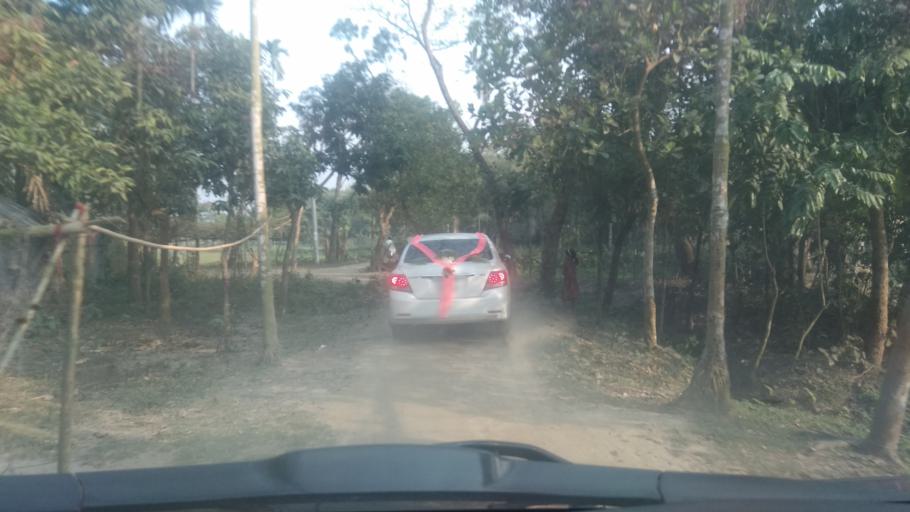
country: BD
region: Dhaka
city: Netrakona
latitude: 24.7736
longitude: 90.6108
